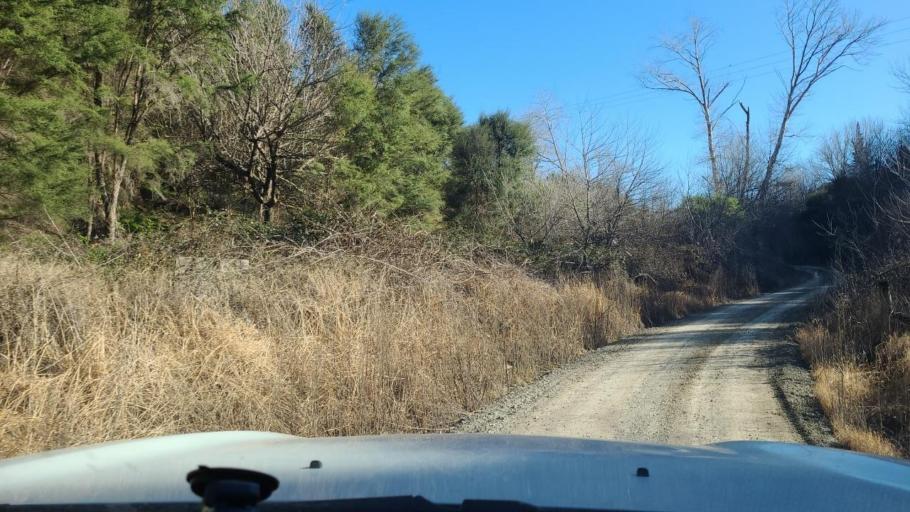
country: NZ
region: Gisborne
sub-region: Gisborne District
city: Gisborne
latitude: -38.6257
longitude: 178.0408
